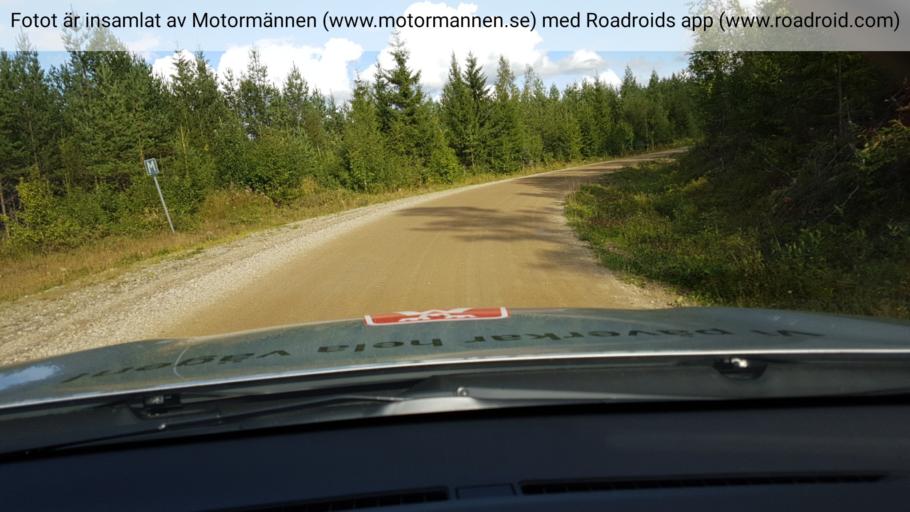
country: SE
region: Jaemtland
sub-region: Ragunda Kommun
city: Hammarstrand
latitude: 63.3389
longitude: 15.8796
